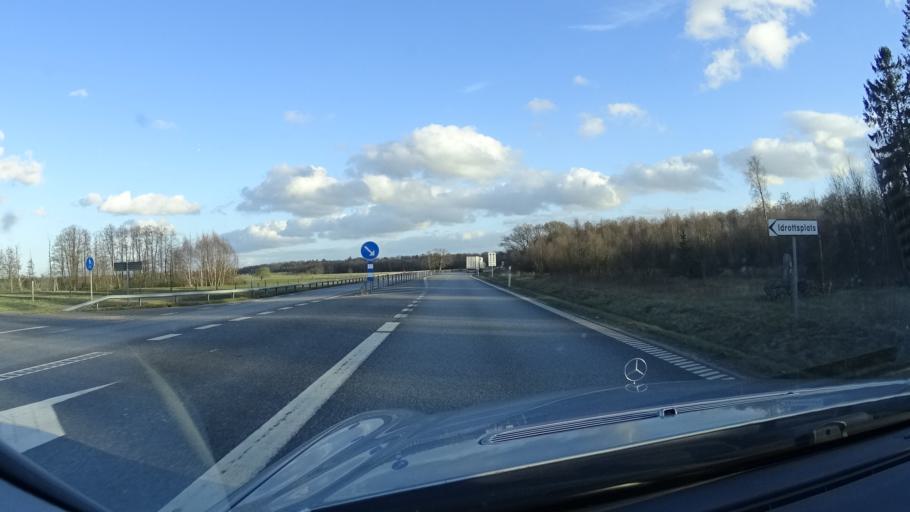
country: SE
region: Skane
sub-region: Hoors Kommun
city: Satofta
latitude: 55.8970
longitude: 13.5231
